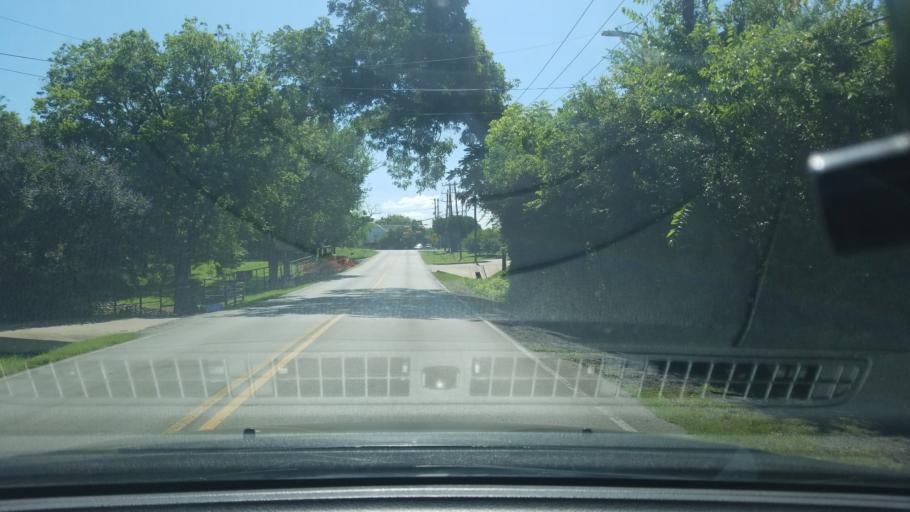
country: US
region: Texas
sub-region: Dallas County
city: Sunnyvale
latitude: 32.7935
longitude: -96.5630
